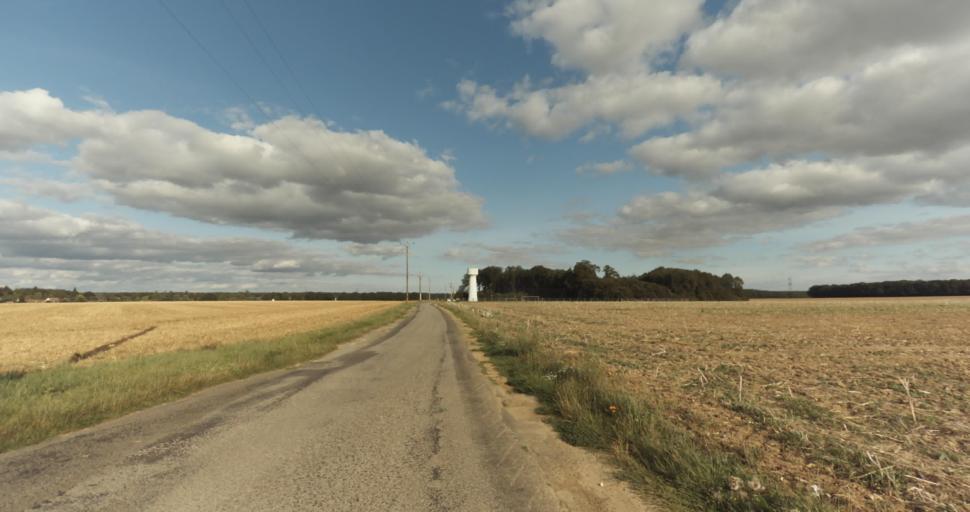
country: FR
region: Haute-Normandie
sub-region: Departement de l'Eure
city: La Couture-Boussey
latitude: 48.8951
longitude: 1.3673
